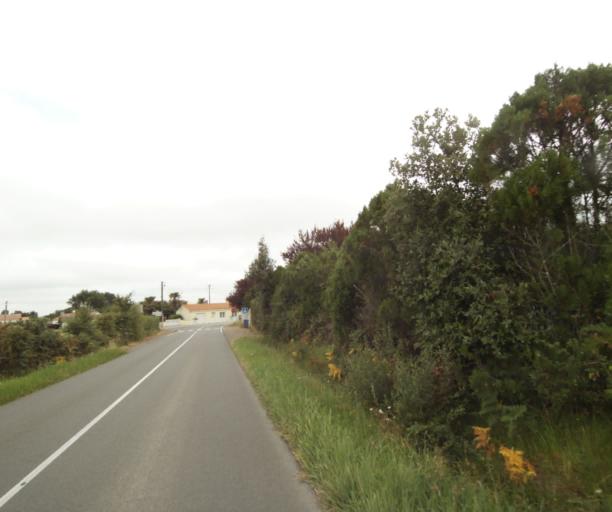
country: FR
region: Pays de la Loire
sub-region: Departement de la Vendee
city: Sainte-Foy
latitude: 46.5139
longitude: -1.6863
